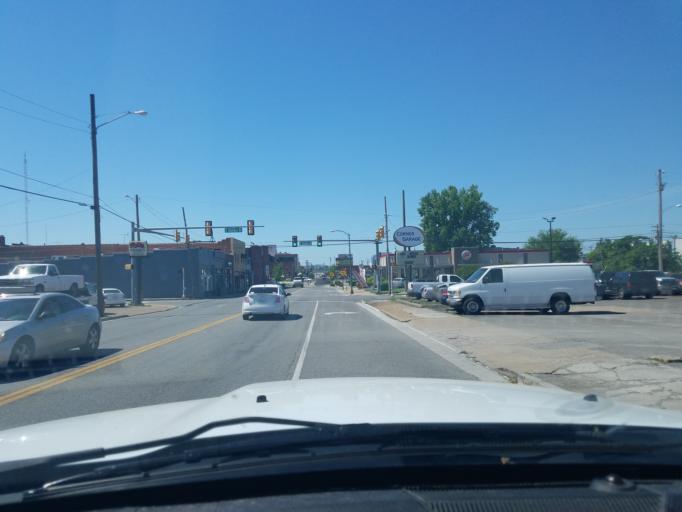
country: US
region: Tennessee
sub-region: Wilson County
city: Lebanon
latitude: 36.2096
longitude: -86.2909
